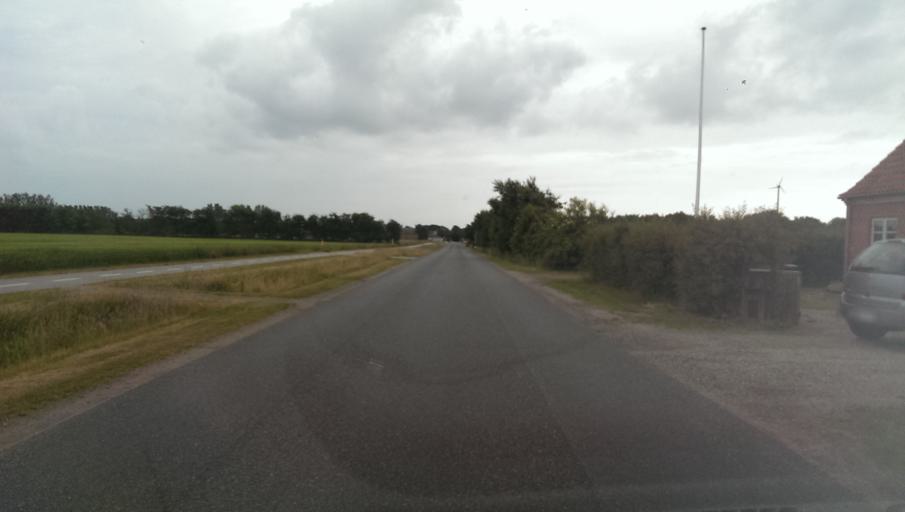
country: DK
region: South Denmark
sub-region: Esbjerg Kommune
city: Bramming
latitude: 55.4411
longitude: 8.7216
